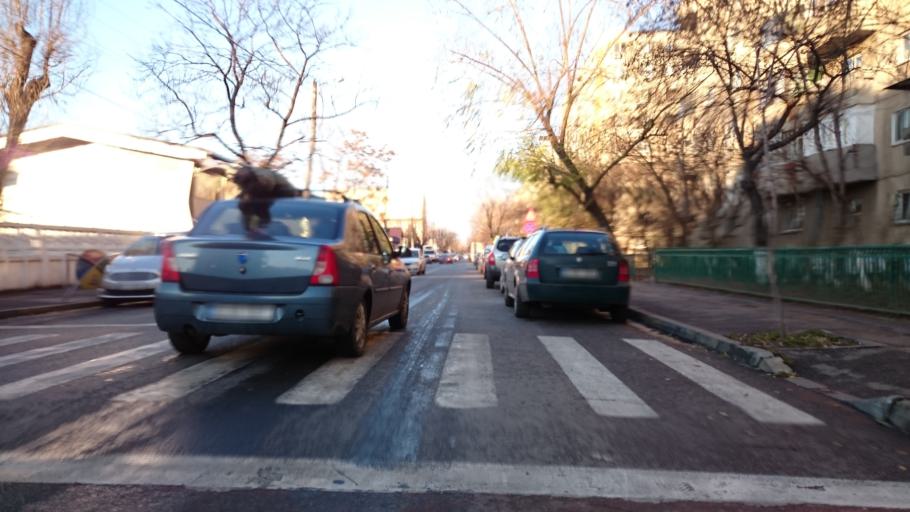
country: RO
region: Bucuresti
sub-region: Municipiul Bucuresti
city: Bucuresti
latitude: 44.4050
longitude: 26.0577
